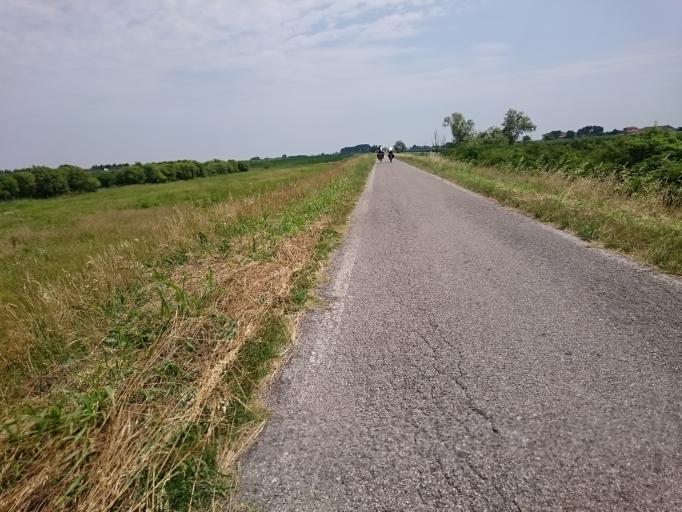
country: IT
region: Veneto
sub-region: Provincia di Venezia
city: Valli
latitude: 45.1883
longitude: 12.2230
